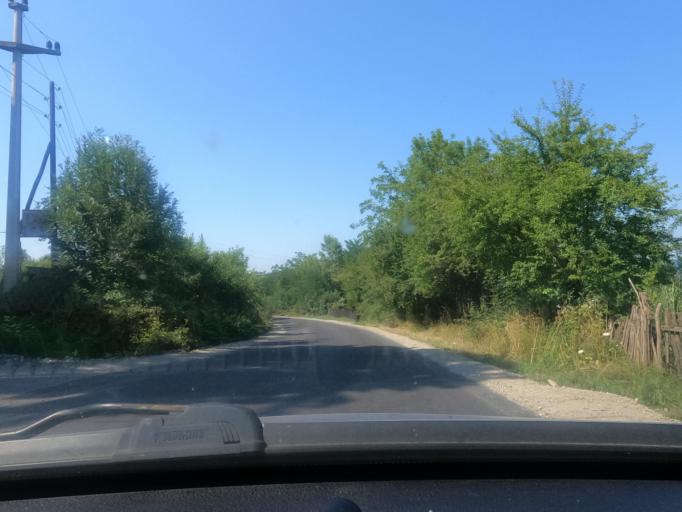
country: RS
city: Kozjak
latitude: 44.5675
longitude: 19.2873
